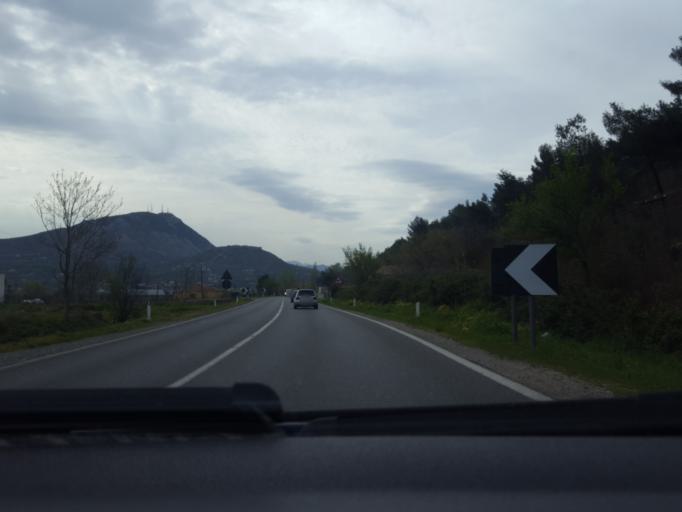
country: AL
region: Lezhe
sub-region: Rrethi i Lezhes
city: Balldreni i Ri
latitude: 41.8008
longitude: 19.6307
